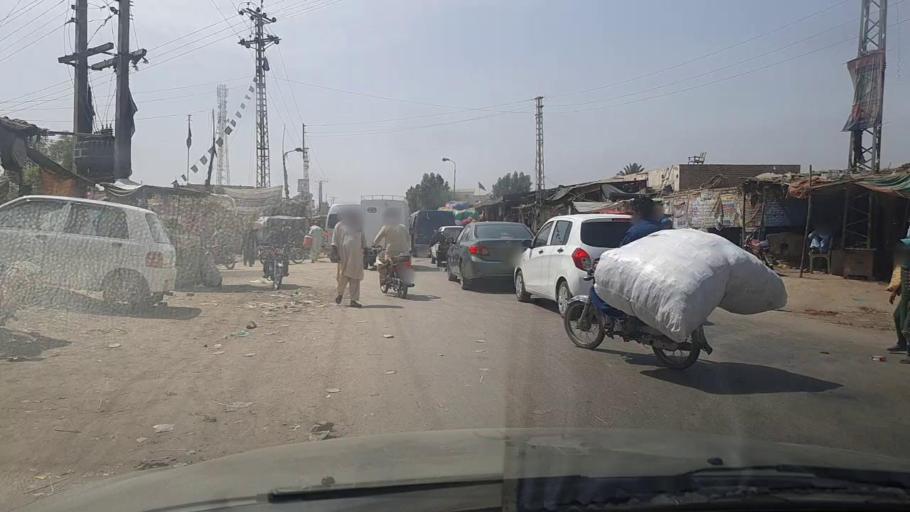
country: PK
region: Sindh
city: Setharja Old
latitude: 27.1314
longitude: 68.5336
